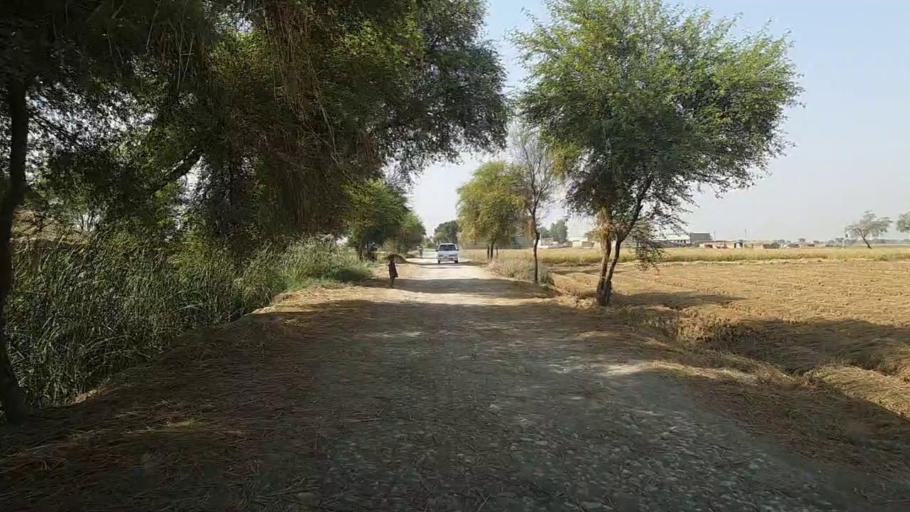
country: PK
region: Sindh
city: Kandhkot
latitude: 28.3952
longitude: 69.2958
